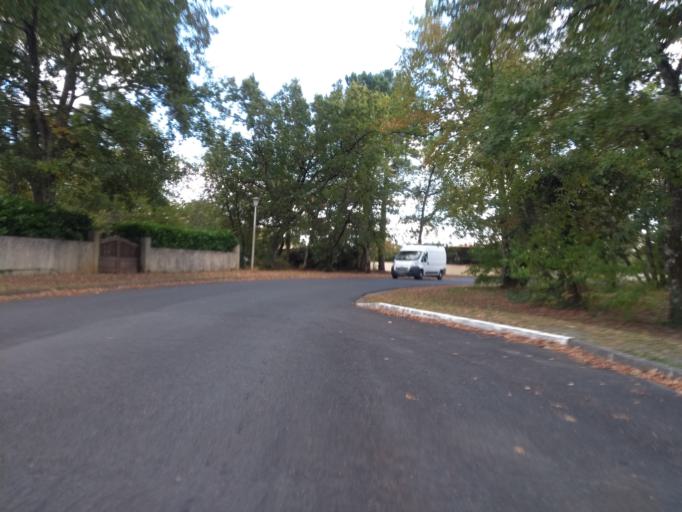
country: FR
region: Aquitaine
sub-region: Departement de la Gironde
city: Cestas
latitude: 44.7353
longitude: -0.6656
